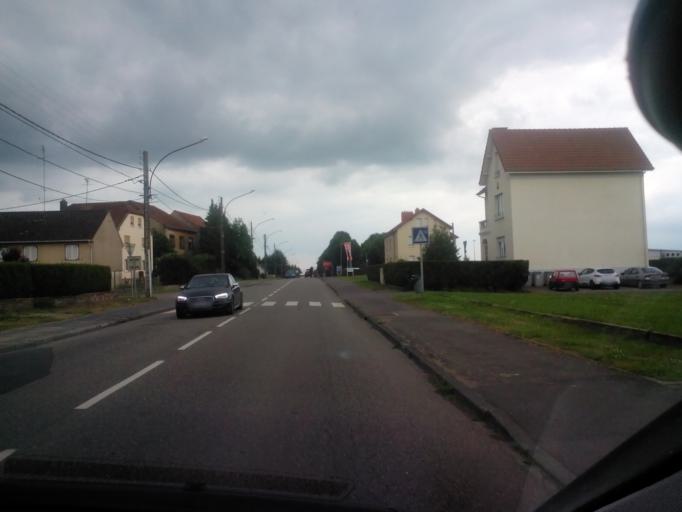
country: FR
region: Lorraine
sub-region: Departement de la Moselle
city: Sarralbe
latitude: 48.9897
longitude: 7.0279
